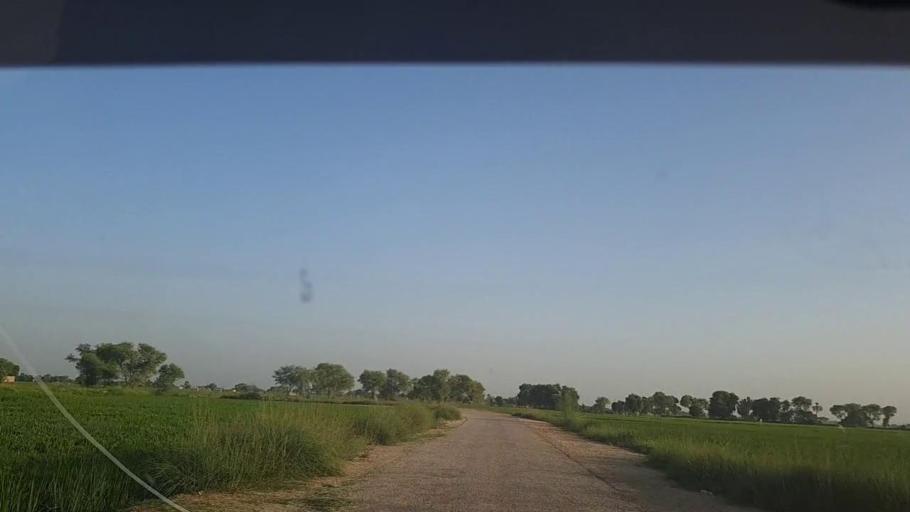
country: PK
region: Sindh
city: Thul
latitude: 28.1268
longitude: 68.8932
